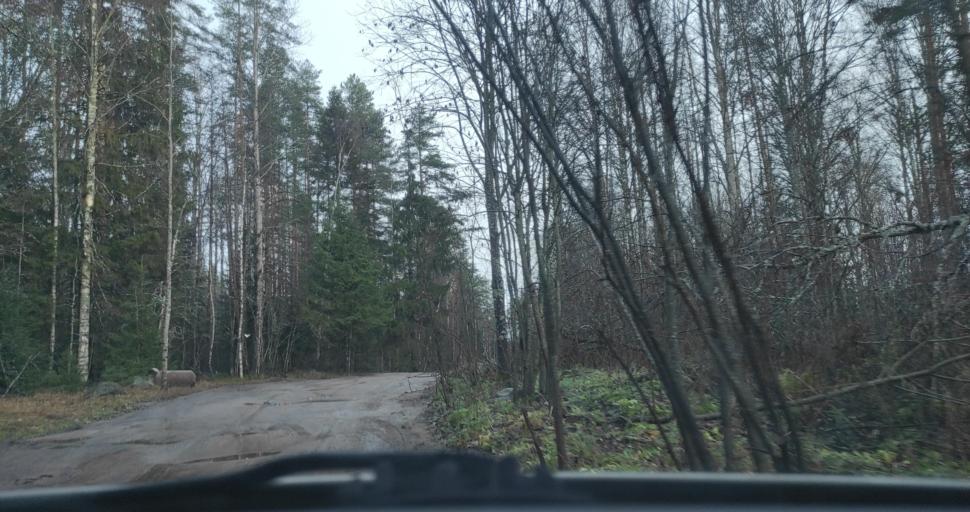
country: RU
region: Republic of Karelia
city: Pitkyaranta
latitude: 61.7431
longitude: 31.3934
